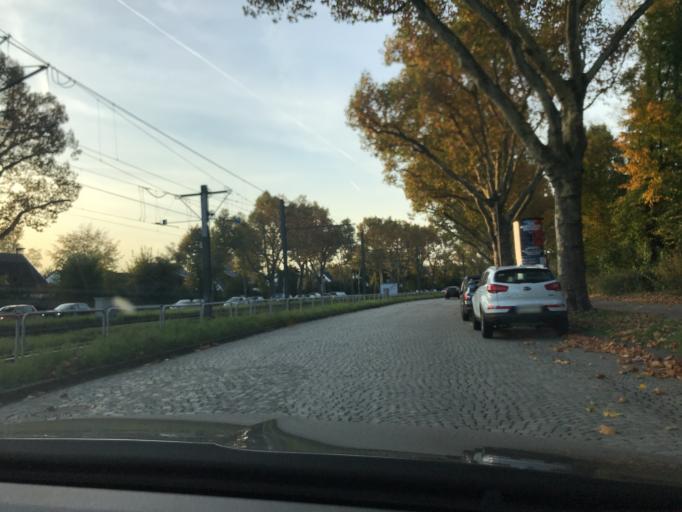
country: DE
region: North Rhine-Westphalia
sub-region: Regierungsbezirk Dusseldorf
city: Dusseldorf
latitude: 51.2537
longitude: 6.7584
